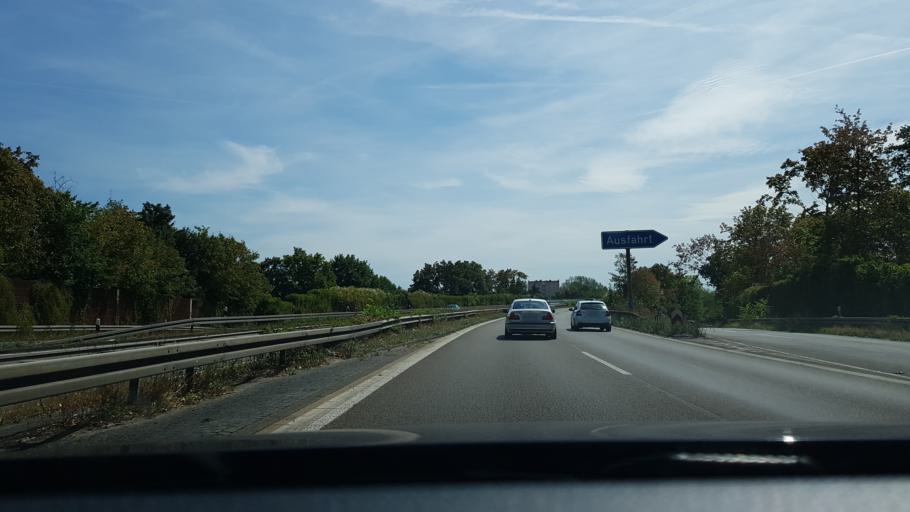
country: DE
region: North Rhine-Westphalia
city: Meiderich
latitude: 51.5043
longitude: 6.7630
